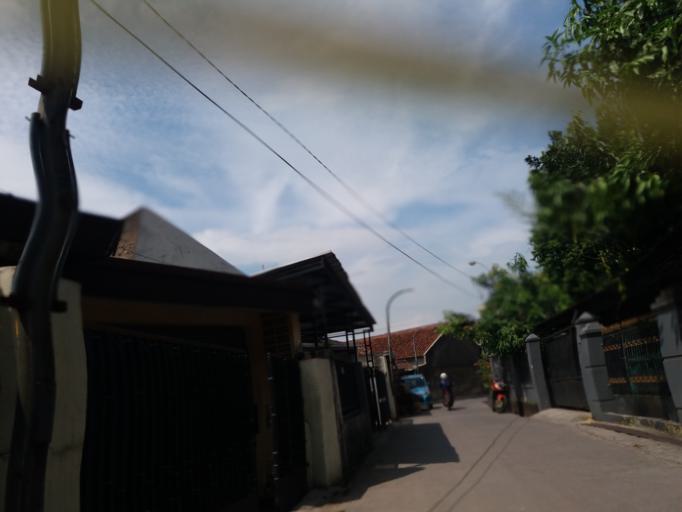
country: ID
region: West Java
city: Bandung
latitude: -6.9197
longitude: 107.6502
